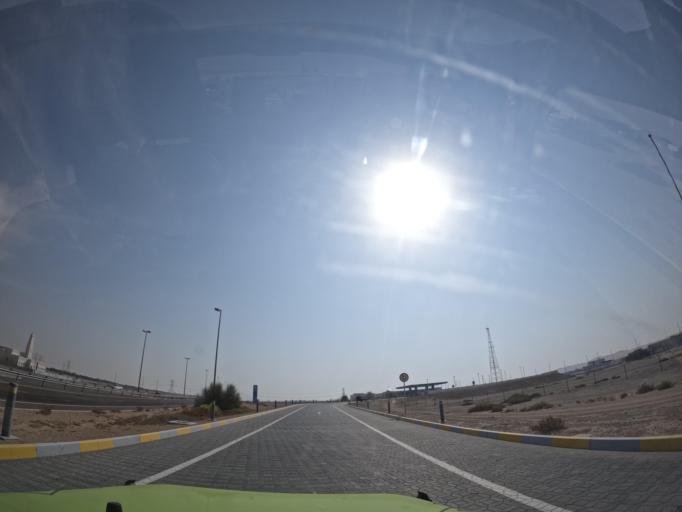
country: OM
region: Al Buraimi
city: Al Buraymi
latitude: 24.5186
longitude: 55.5133
